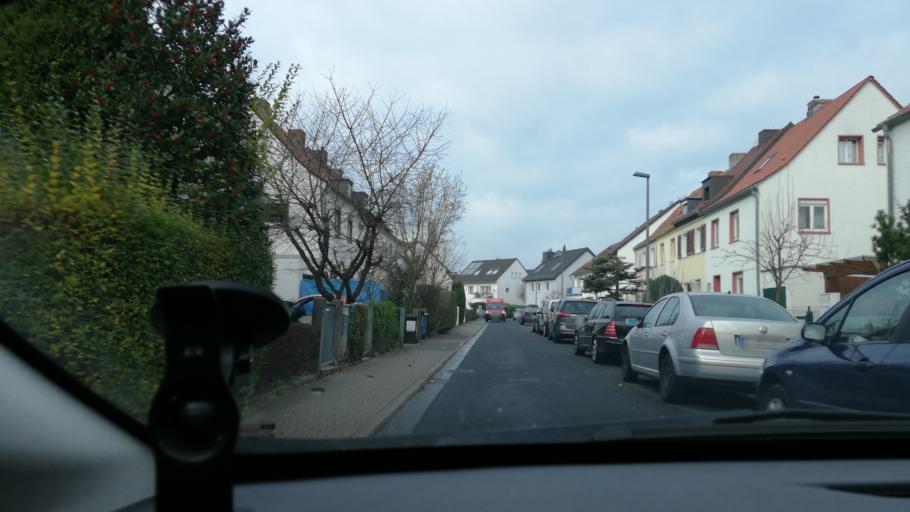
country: DE
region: Hesse
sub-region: Regierungsbezirk Darmstadt
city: Frankfurt am Main
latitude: 50.1456
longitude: 8.6990
